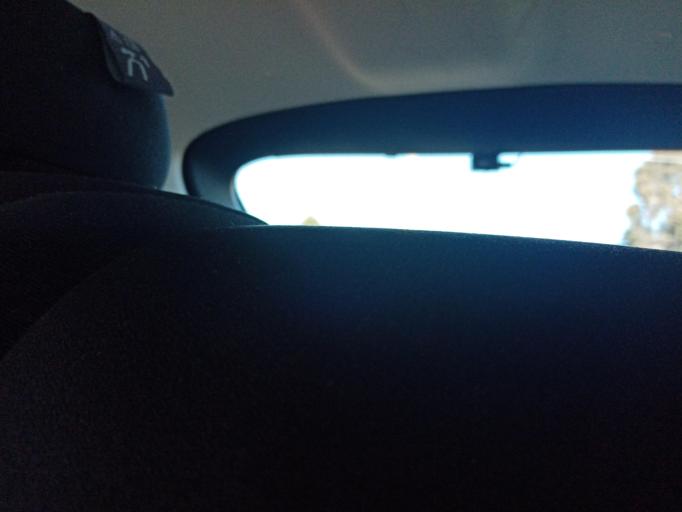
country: AU
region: Western Australia
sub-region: City of Cockburn
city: South Lake
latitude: -32.1259
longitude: 115.8394
